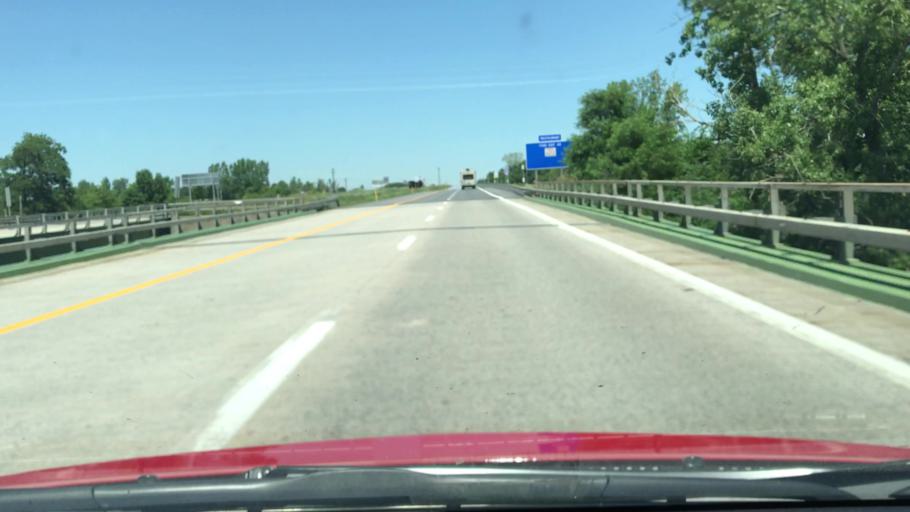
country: US
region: New York
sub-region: Clinton County
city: Champlain
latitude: 44.9871
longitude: -73.4573
